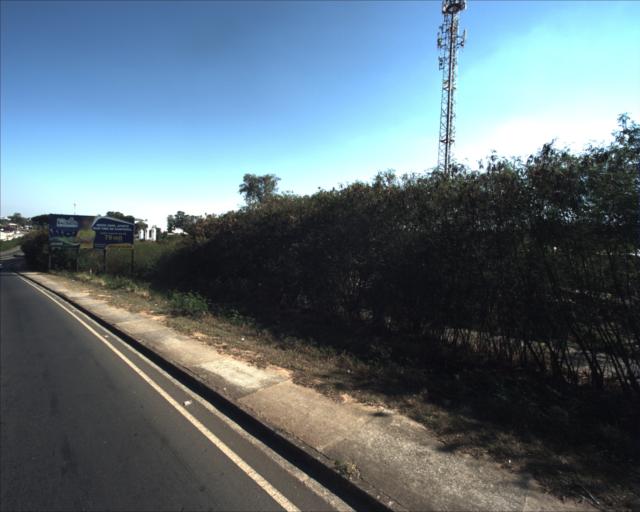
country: BR
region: Sao Paulo
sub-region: Sorocaba
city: Sorocaba
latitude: -23.4621
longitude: -47.4228
